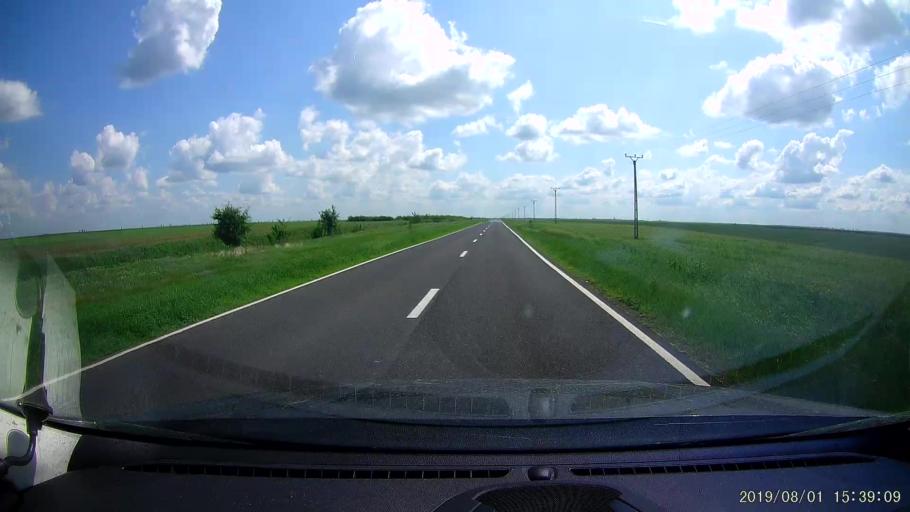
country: RO
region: Braila
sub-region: Comuna Insuratei
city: Insuratei
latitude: 44.8643
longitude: 27.5653
